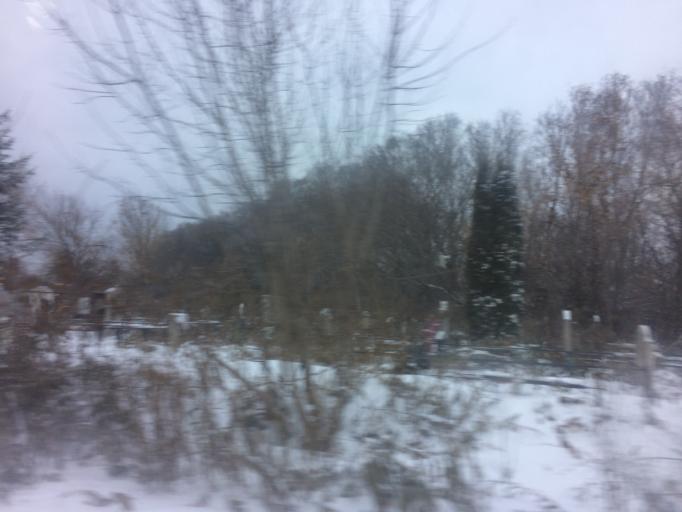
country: RU
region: Tula
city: Tula
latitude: 54.1440
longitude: 37.6517
